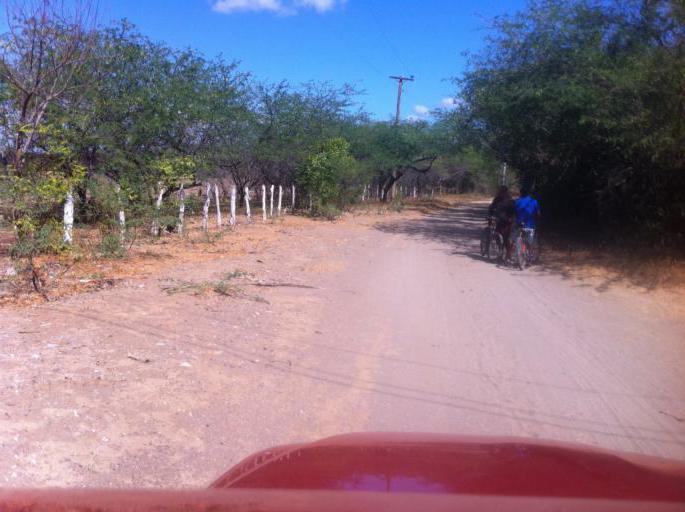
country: NI
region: Carazo
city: Santa Teresa
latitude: 11.6078
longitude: -86.3057
